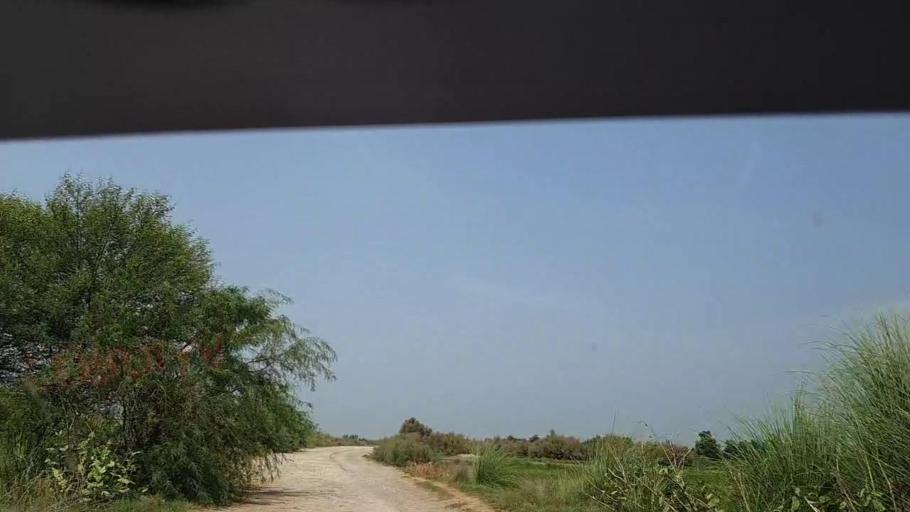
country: PK
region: Sindh
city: Adilpur
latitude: 27.8860
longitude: 69.2578
